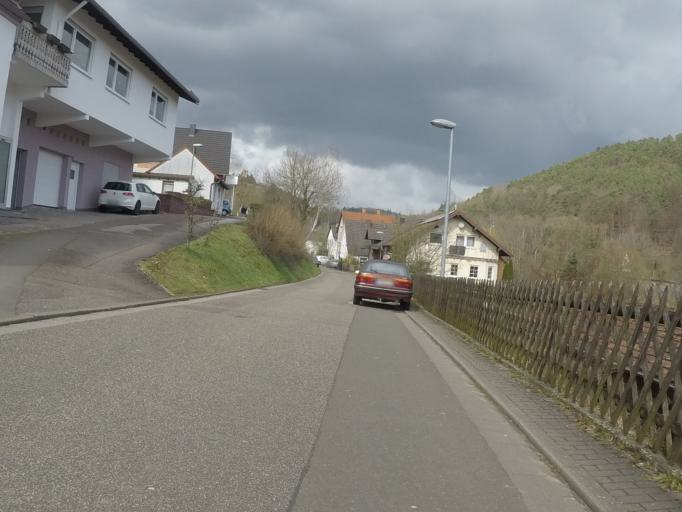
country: DE
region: Rheinland-Pfalz
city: Munchweiler an der Rodalbe
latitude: 49.2202
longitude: 7.6988
